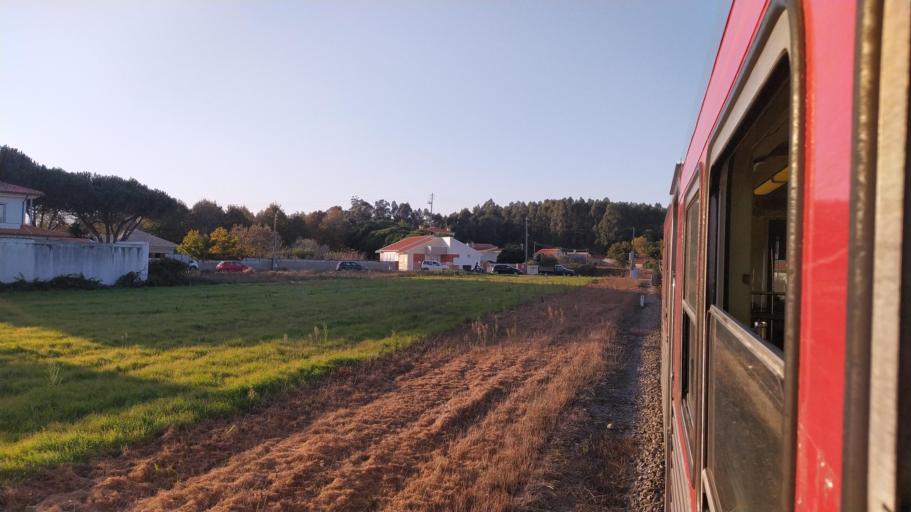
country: PT
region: Aveiro
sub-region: Aveiro
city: Eixo
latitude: 40.6387
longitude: -8.5854
